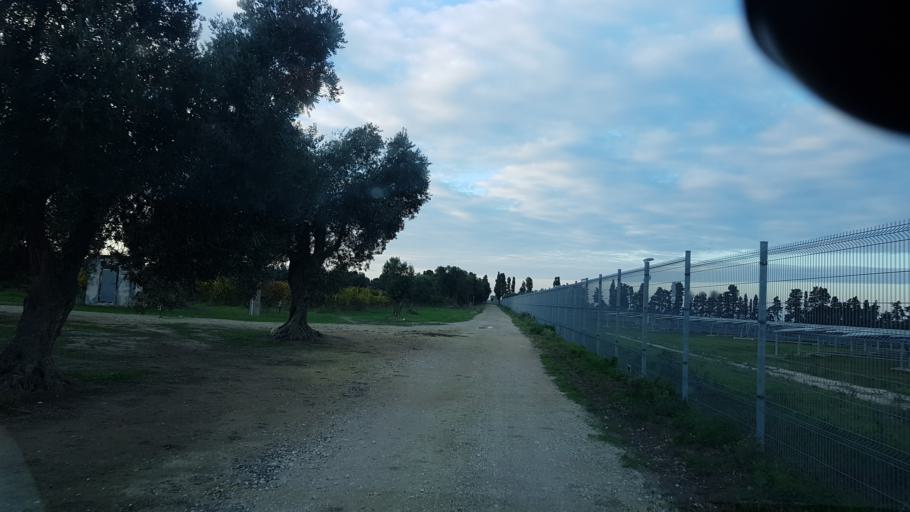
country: IT
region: Apulia
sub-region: Provincia di Brindisi
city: La Rosa
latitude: 40.5926
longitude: 17.9858
